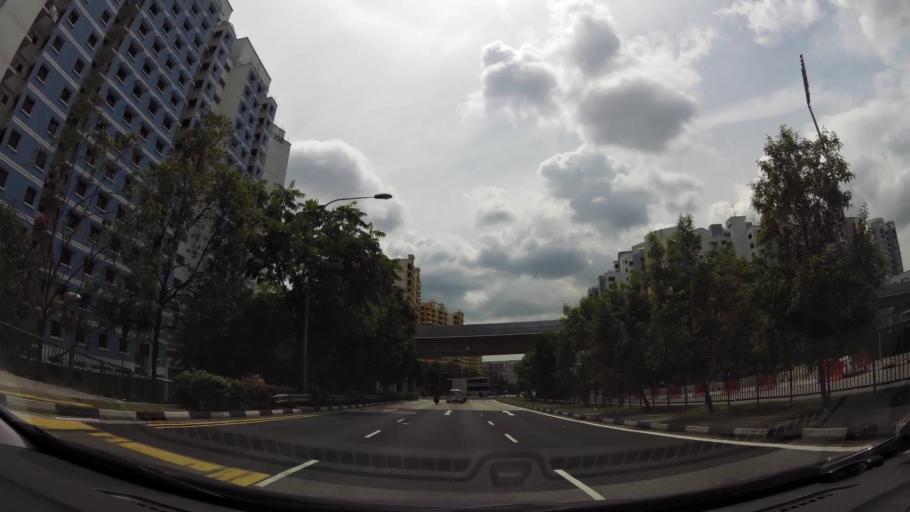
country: MY
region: Johor
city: Johor Bahru
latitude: 1.3384
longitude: 103.6958
